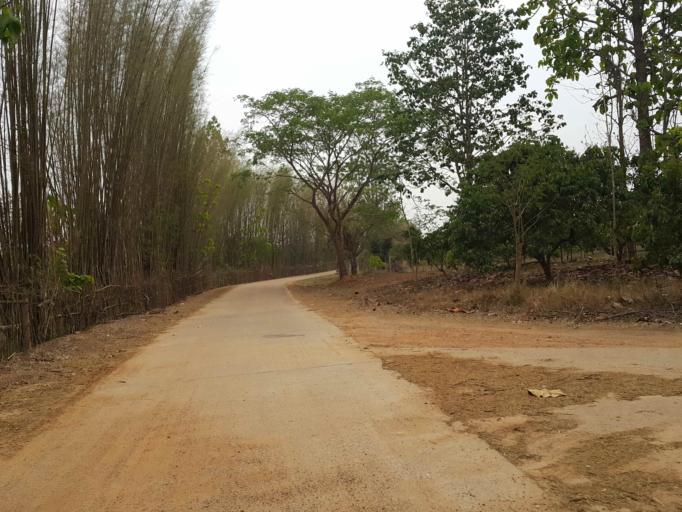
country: TH
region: Chiang Mai
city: San Sai
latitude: 18.9399
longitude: 99.0100
